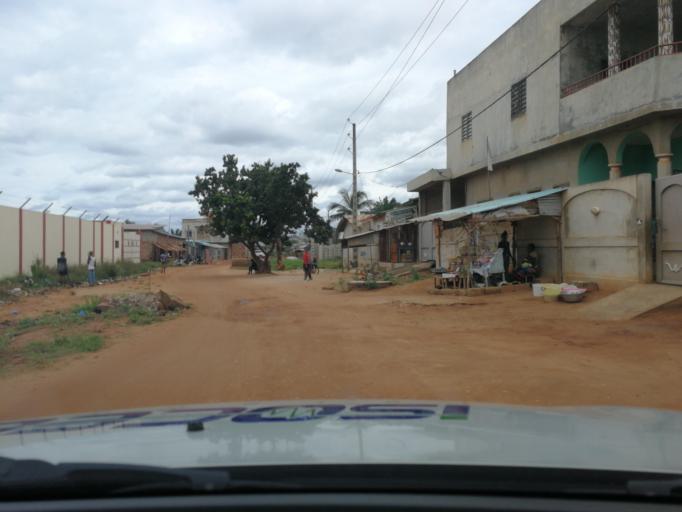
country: BJ
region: Atlantique
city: Abomey-Calavi
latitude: 6.4315
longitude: 2.3068
